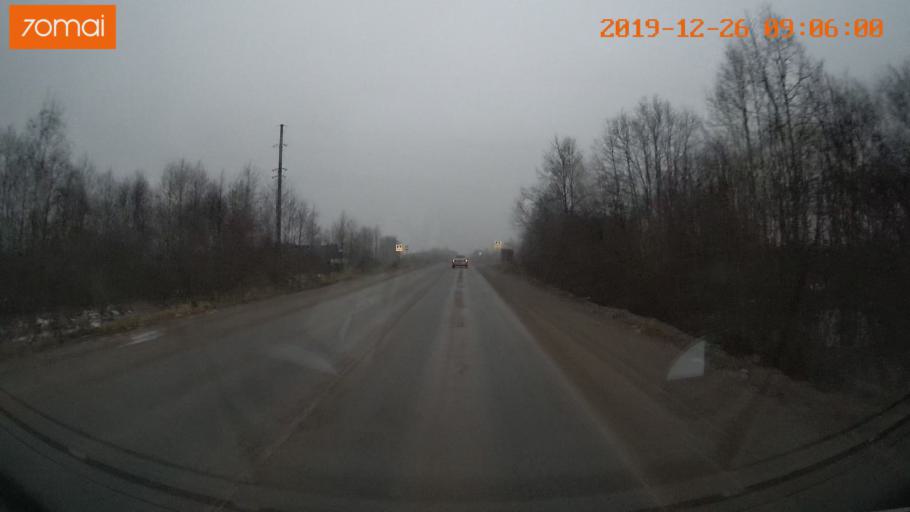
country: RU
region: Vologda
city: Gryazovets
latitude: 58.8316
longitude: 40.2553
